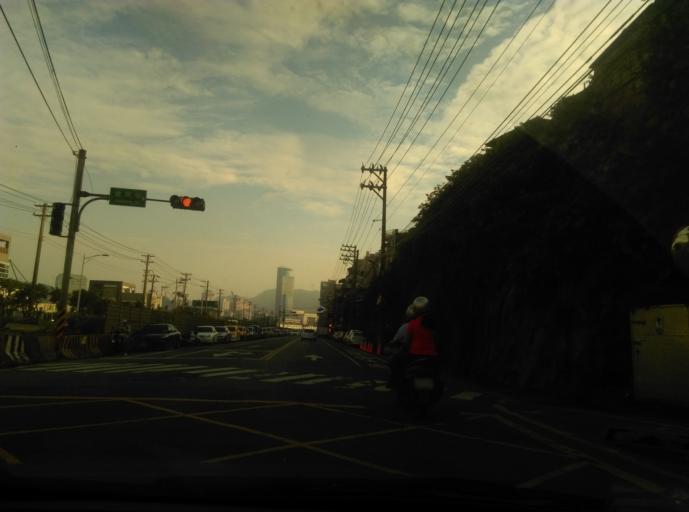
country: TW
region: Taiwan
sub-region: Keelung
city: Keelung
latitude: 25.1412
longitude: 121.7389
